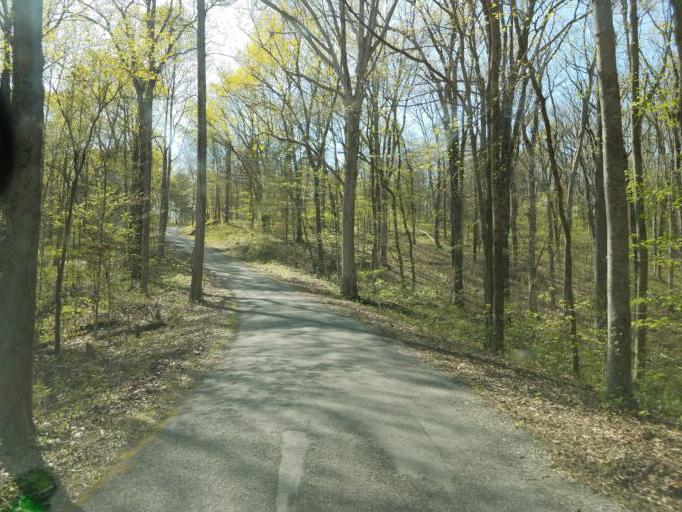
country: US
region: Kentucky
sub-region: Barren County
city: Cave City
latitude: 37.1253
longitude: -86.0935
